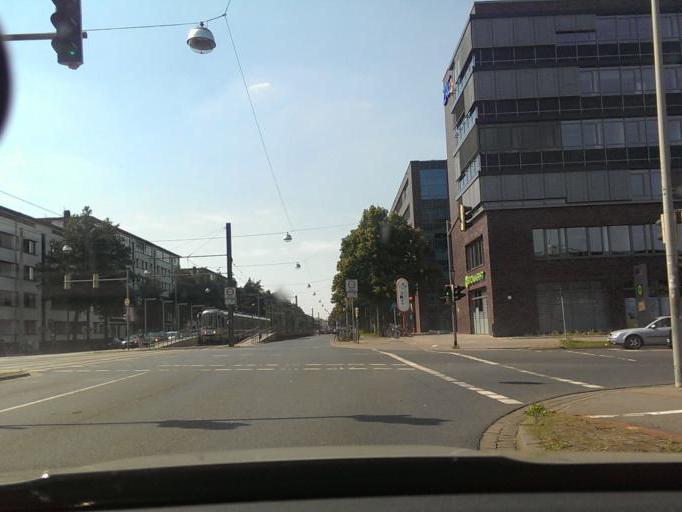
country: DE
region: Lower Saxony
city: Hannover
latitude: 52.4032
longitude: 9.7921
